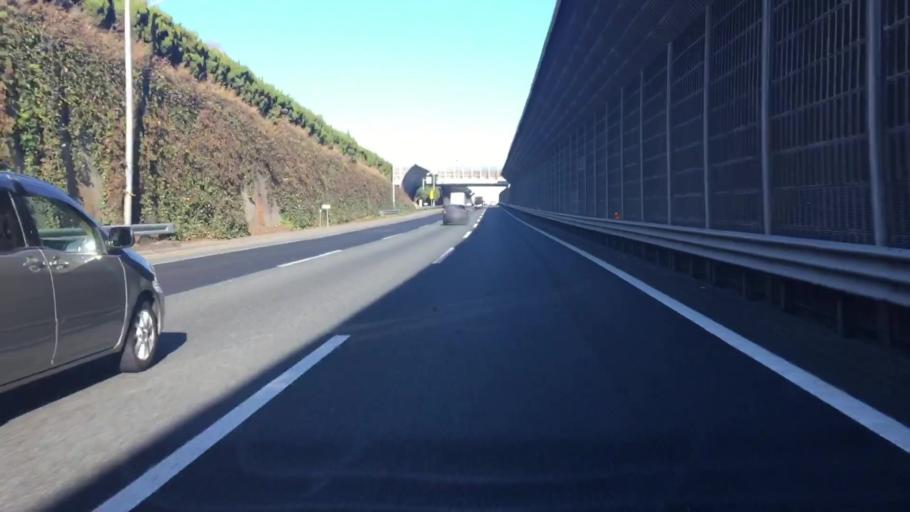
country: JP
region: Chiba
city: Chiba
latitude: 35.6436
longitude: 140.0796
